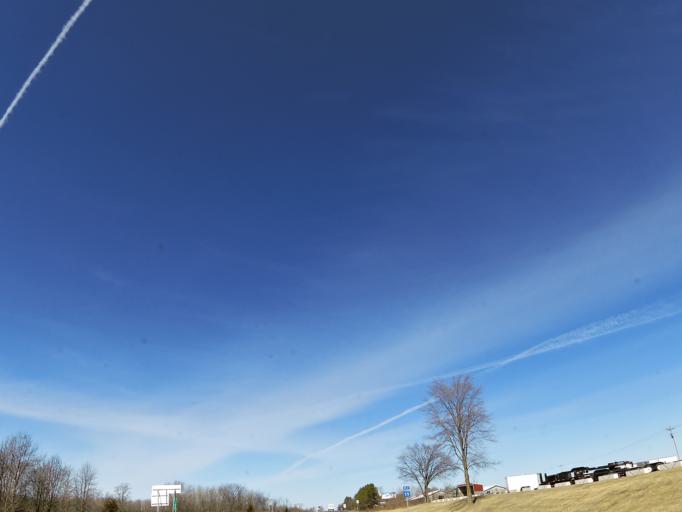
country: US
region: Minnesota
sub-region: Wright County
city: Buffalo
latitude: 45.1382
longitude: -93.8291
